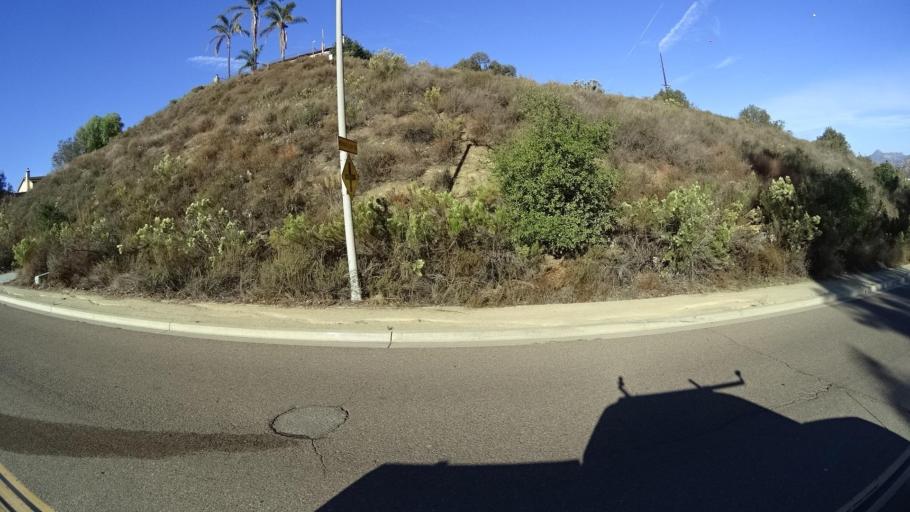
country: US
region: California
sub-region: San Diego County
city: Lakeside
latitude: 32.8499
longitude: -116.9041
